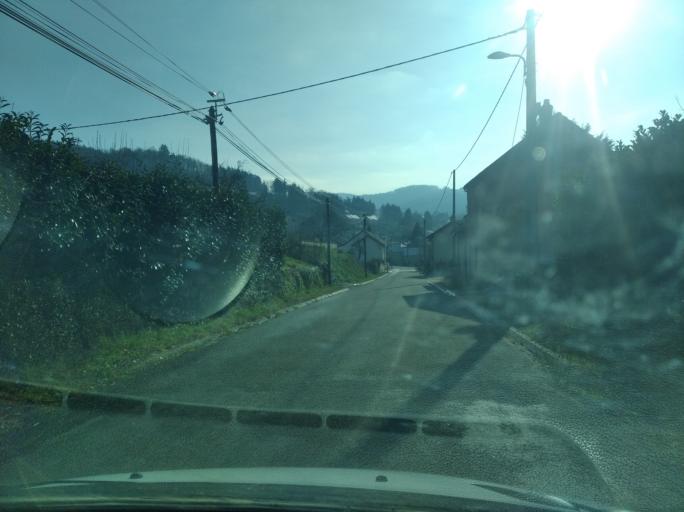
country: FR
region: Auvergne
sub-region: Departement de l'Allier
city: Le Mayet-de-Montagne
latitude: 46.1619
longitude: 3.7337
